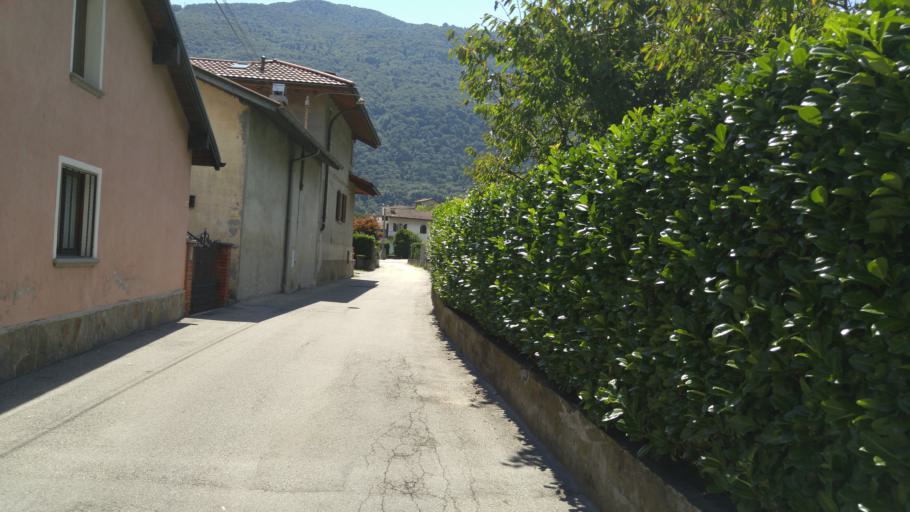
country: IT
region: Piedmont
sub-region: Provincia Verbano-Cusio-Ossola
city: Cannobio
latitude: 46.0651
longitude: 8.6878
